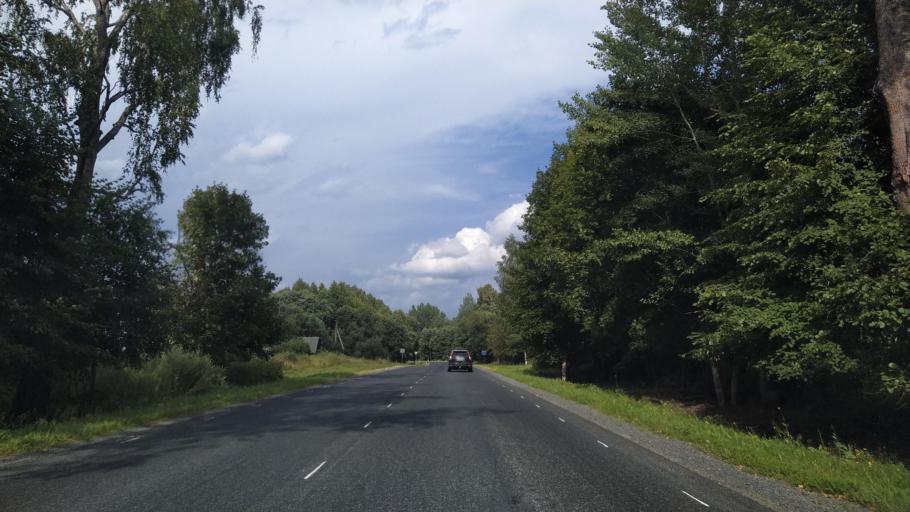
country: RU
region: Pskov
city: Porkhov
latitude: 57.8405
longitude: 29.5424
